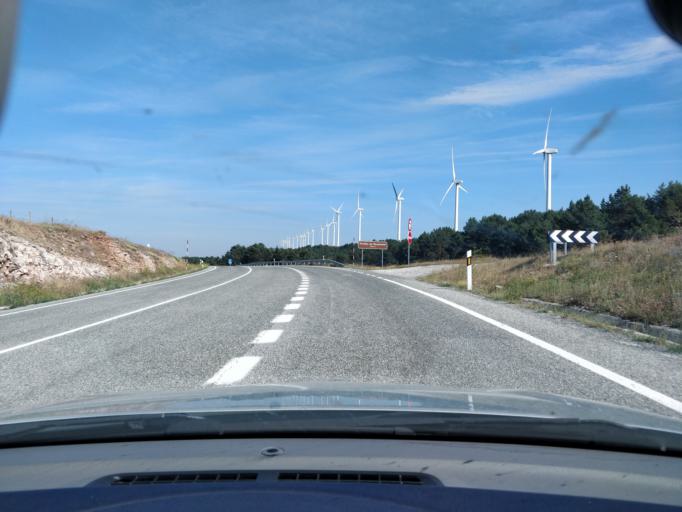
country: ES
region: Castille and Leon
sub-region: Provincia de Burgos
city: Medina de Pomar
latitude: 42.9322
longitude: -3.6583
